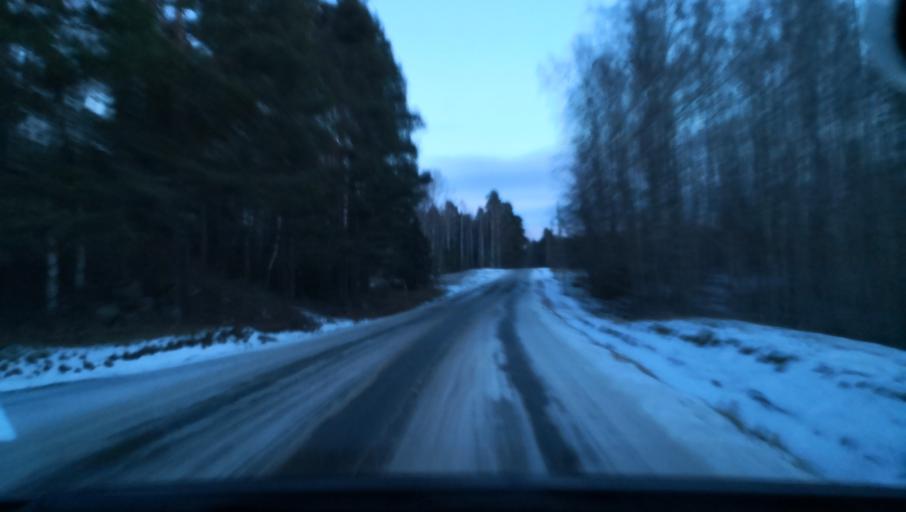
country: SE
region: Soedermanland
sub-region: Katrineholms Kommun
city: Katrineholm
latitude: 59.0824
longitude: 16.2310
